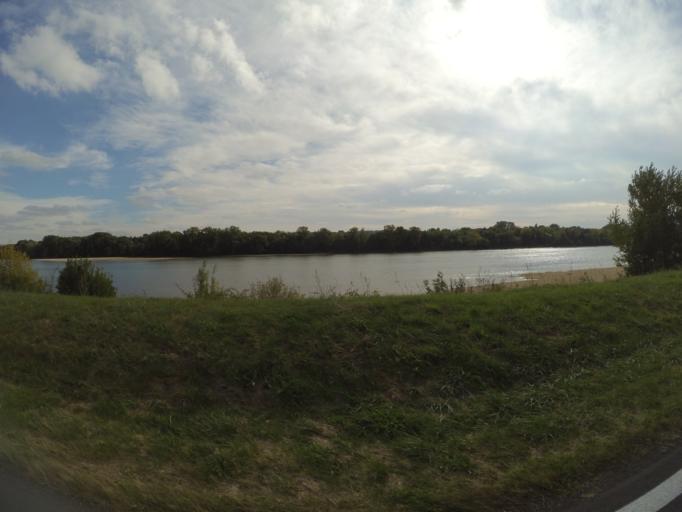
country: FR
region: Centre
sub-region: Departement d'Indre-et-Loire
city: Huismes
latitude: 47.2611
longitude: 0.2621
